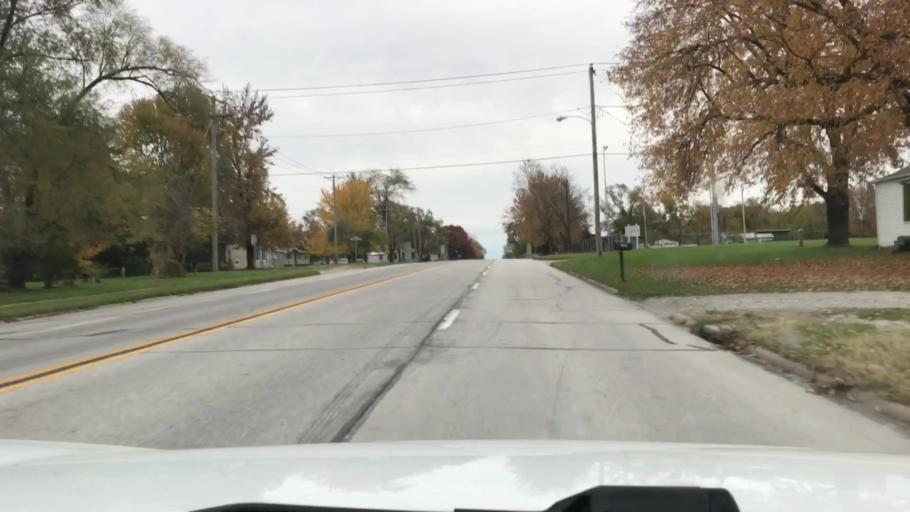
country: US
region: Iowa
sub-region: Lee County
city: Keokuk
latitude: 40.3901
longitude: -91.4099
